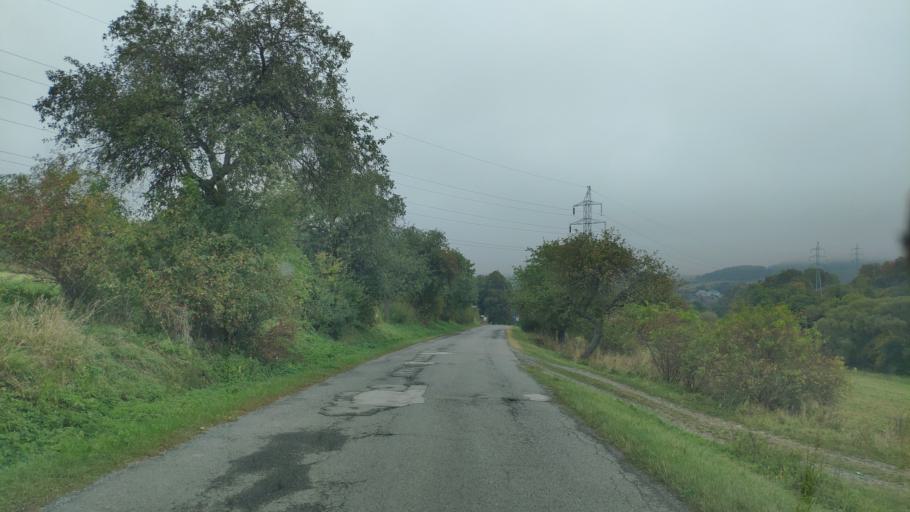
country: SK
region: Presovsky
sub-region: Okres Presov
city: Presov
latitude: 48.8738
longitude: 21.4395
